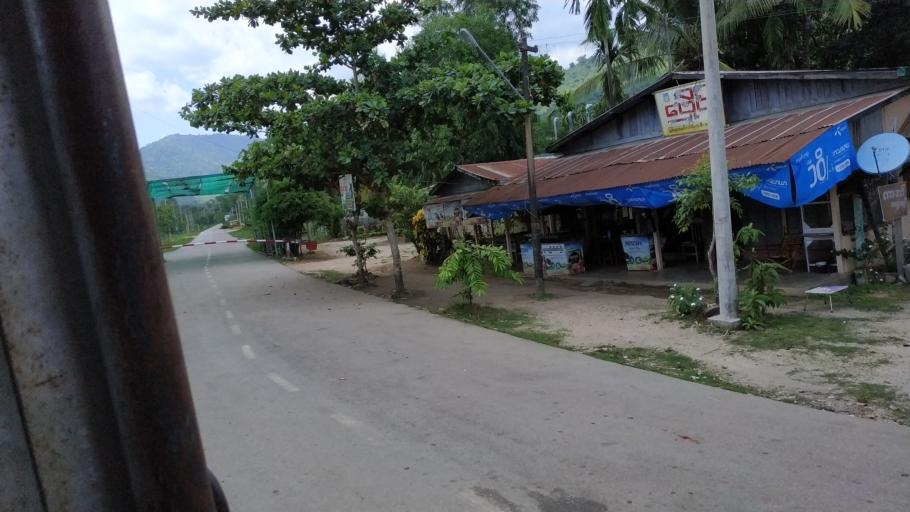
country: MM
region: Mon
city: Kyaikto
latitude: 17.4055
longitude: 97.0741
